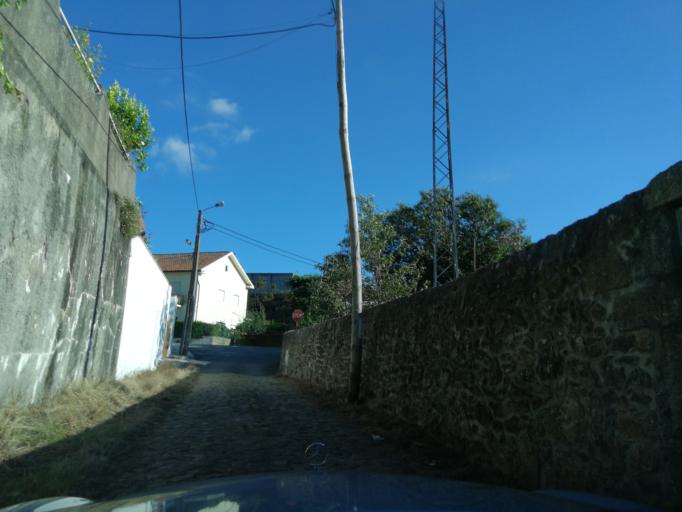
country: PT
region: Braga
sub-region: Braga
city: Braga
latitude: 41.5469
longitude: -8.3941
